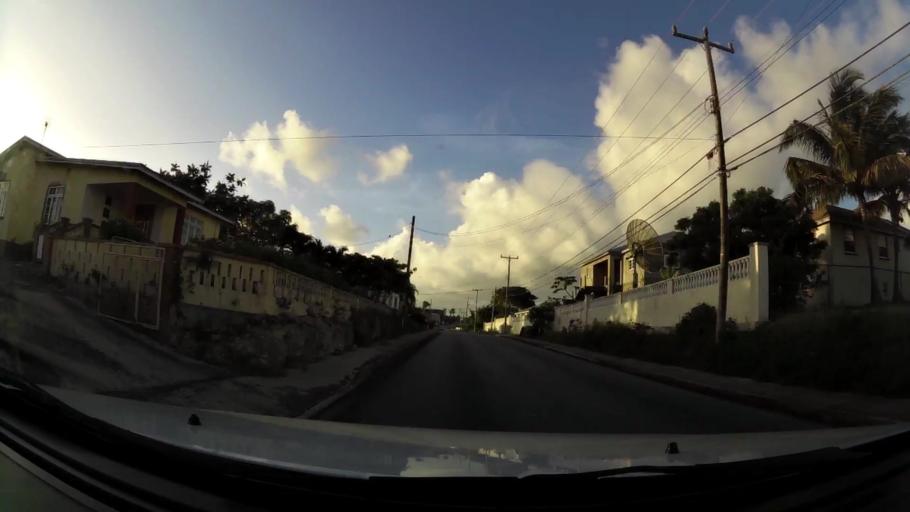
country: BB
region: Saint Philip
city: Crane
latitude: 13.1009
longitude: -59.4656
